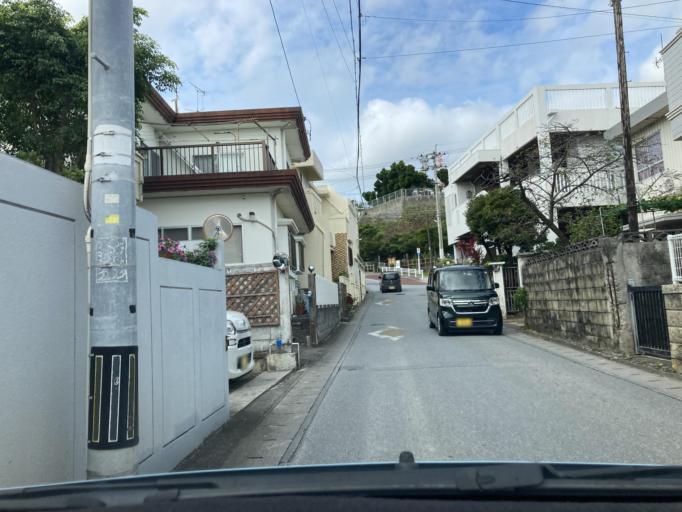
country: JP
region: Okinawa
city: Ginowan
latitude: 26.2033
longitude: 127.7528
